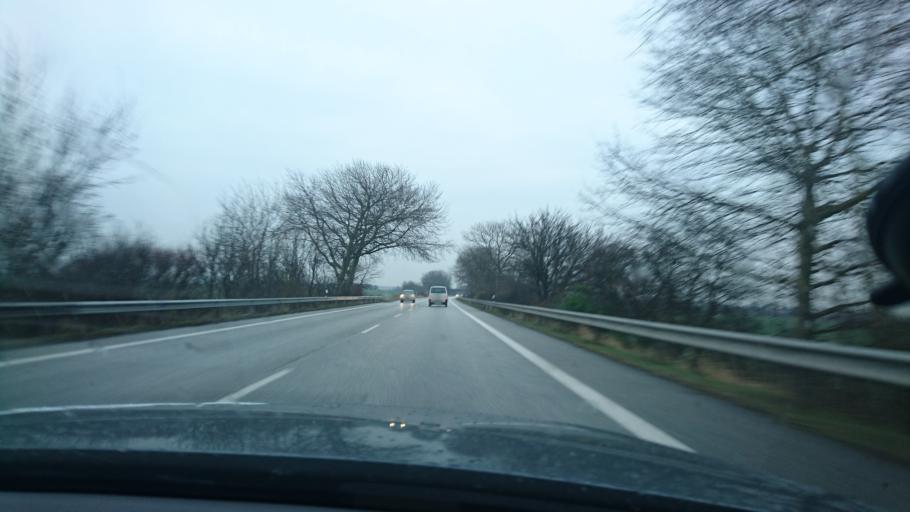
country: DE
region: Schleswig-Holstein
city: Grossenbrode
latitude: 54.3681
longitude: 11.0459
